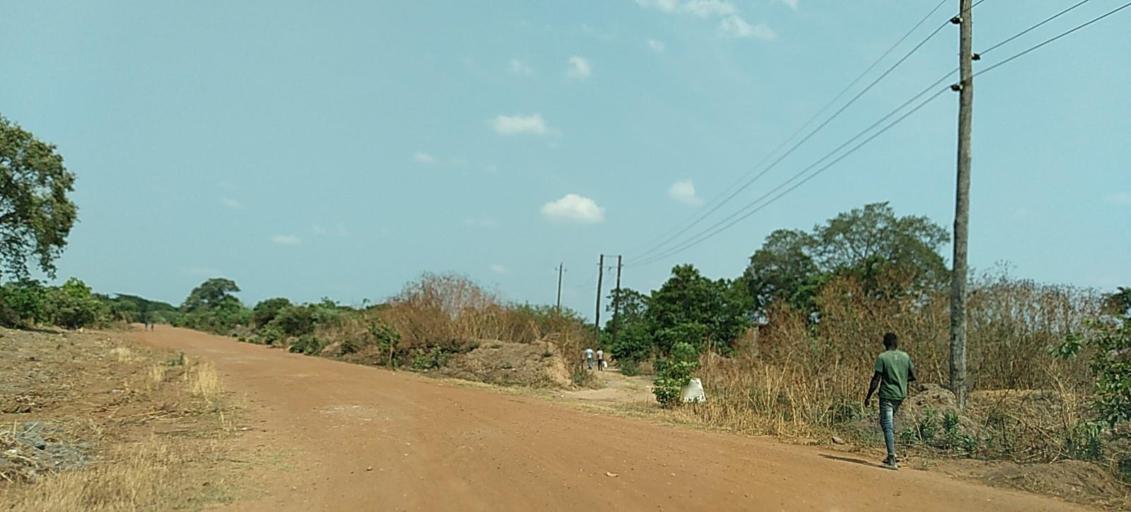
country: ZM
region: Copperbelt
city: Luanshya
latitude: -13.0925
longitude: 28.3079
